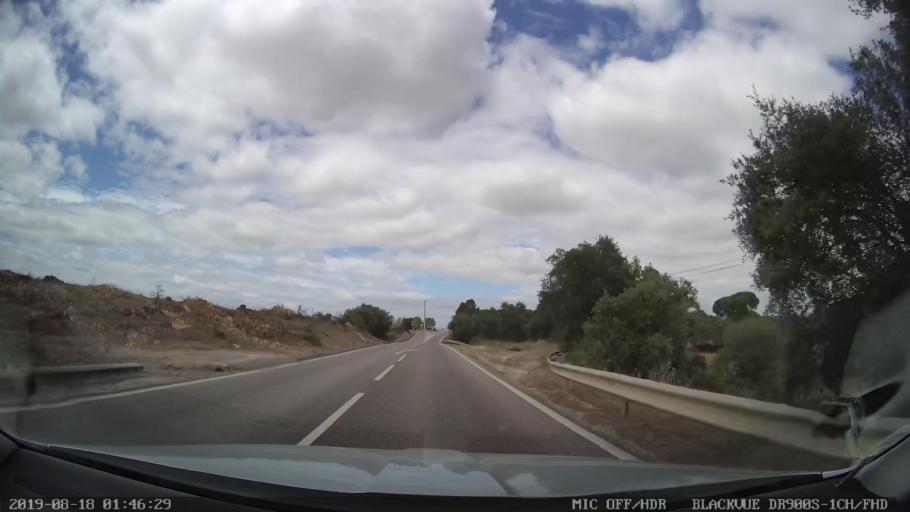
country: PT
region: Santarem
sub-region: Benavente
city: Benavente
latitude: 38.9349
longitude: -8.7821
